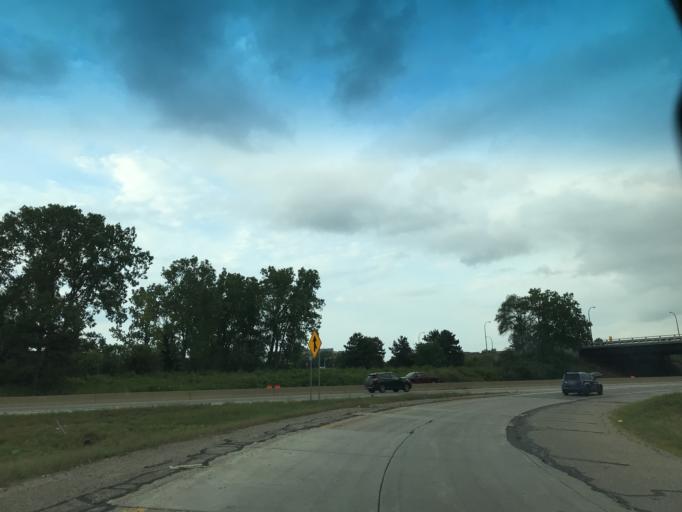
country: US
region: Michigan
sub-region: Washtenaw County
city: Ann Arbor
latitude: 42.2363
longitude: -83.7408
